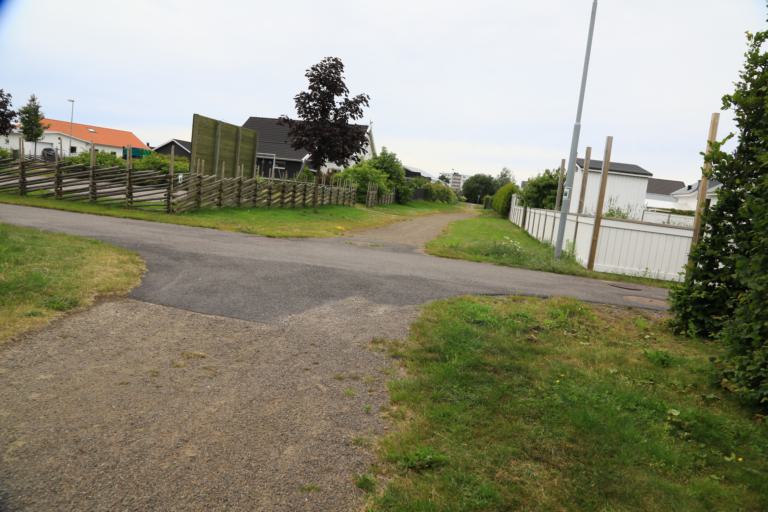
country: SE
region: Halland
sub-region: Varbergs Kommun
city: Traslovslage
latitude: 57.0855
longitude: 12.2822
